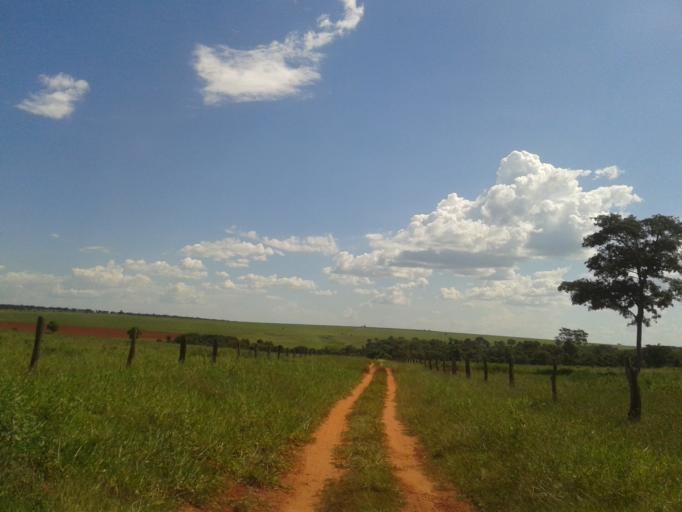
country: BR
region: Minas Gerais
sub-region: Santa Vitoria
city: Santa Vitoria
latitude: -19.1142
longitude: -50.4994
